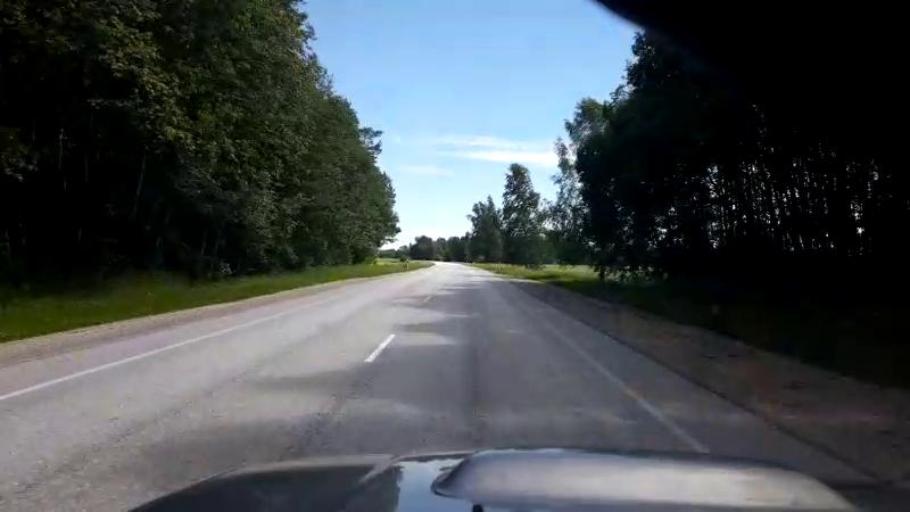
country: EE
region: Laeaene-Virumaa
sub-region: Rakke vald
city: Rakke
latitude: 58.9485
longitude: 26.1828
